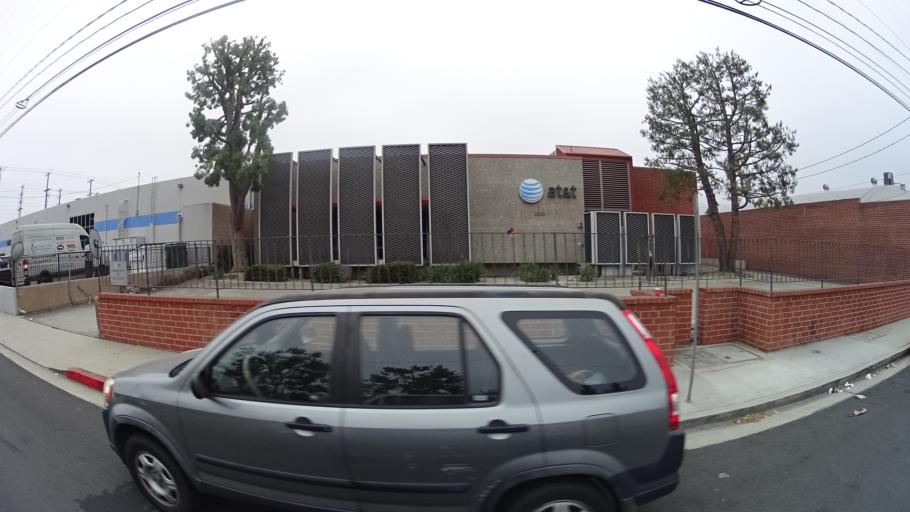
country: US
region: California
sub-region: Los Angeles County
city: Burbank
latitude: 34.1956
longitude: -118.3436
